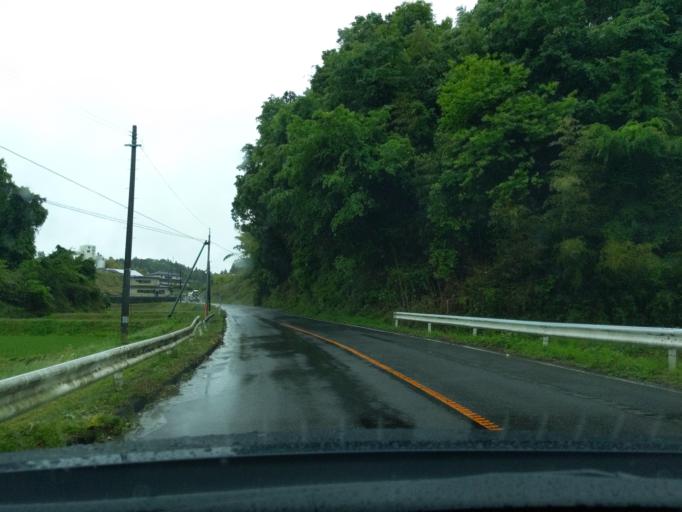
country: JP
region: Fukushima
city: Nihommatsu
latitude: 37.5252
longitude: 140.4859
